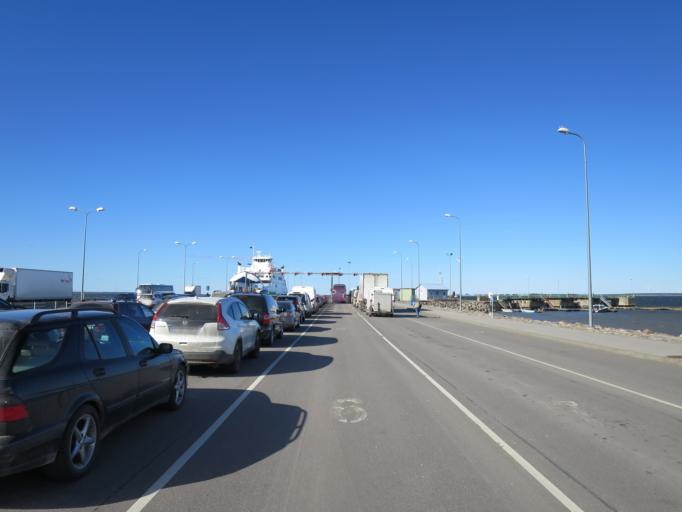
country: EE
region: Laeaene
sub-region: Lihula vald
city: Lihula
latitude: 58.5737
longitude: 23.5105
